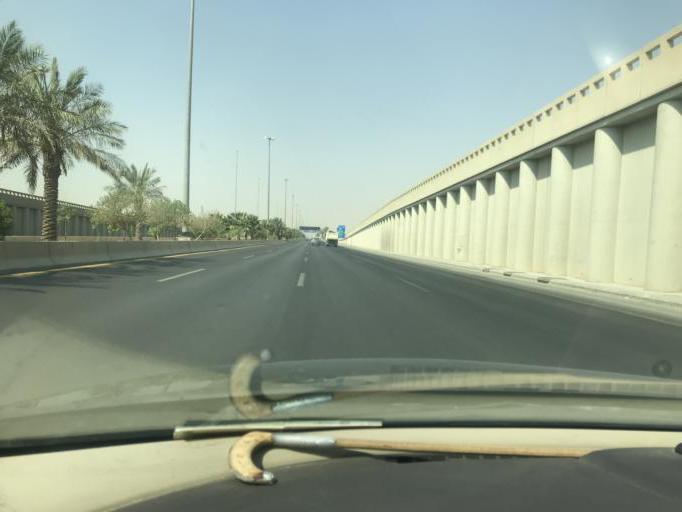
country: SA
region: Ar Riyad
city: Riyadh
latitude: 24.8429
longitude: 46.6524
